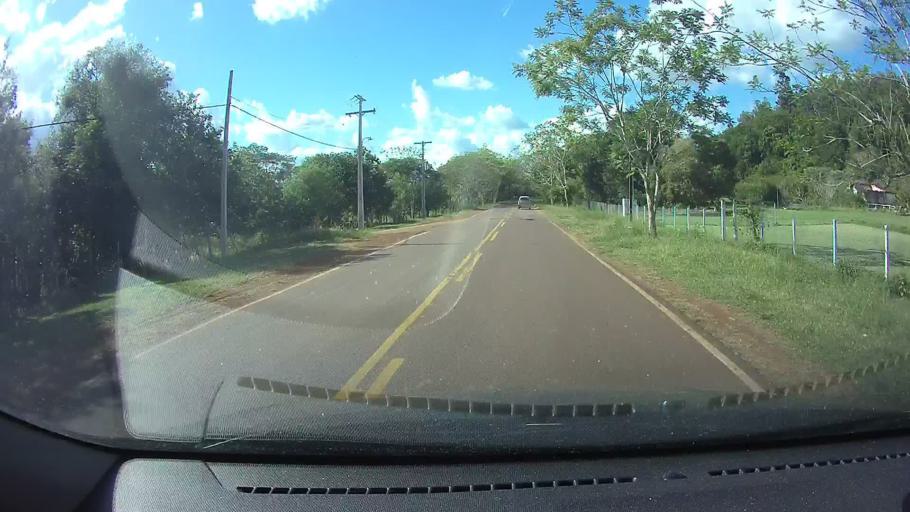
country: PY
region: Cordillera
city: Itacurubi de la Cordillera
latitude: -25.4788
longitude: -56.8808
